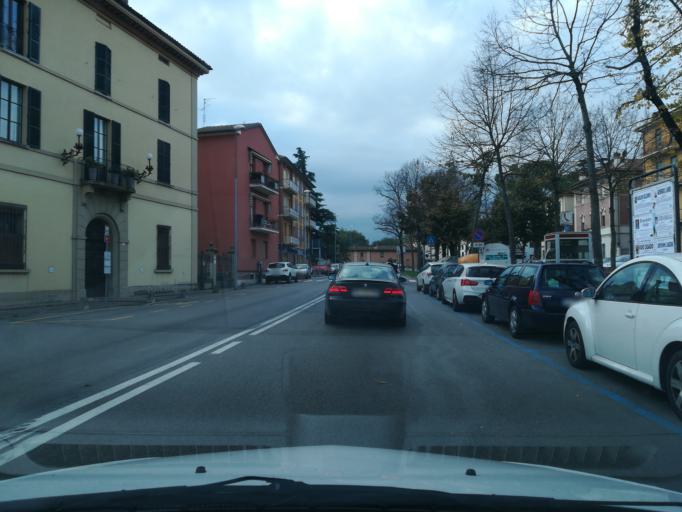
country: IT
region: Emilia-Romagna
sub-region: Provincia di Bologna
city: Imola
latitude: 44.3515
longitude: 11.7200
